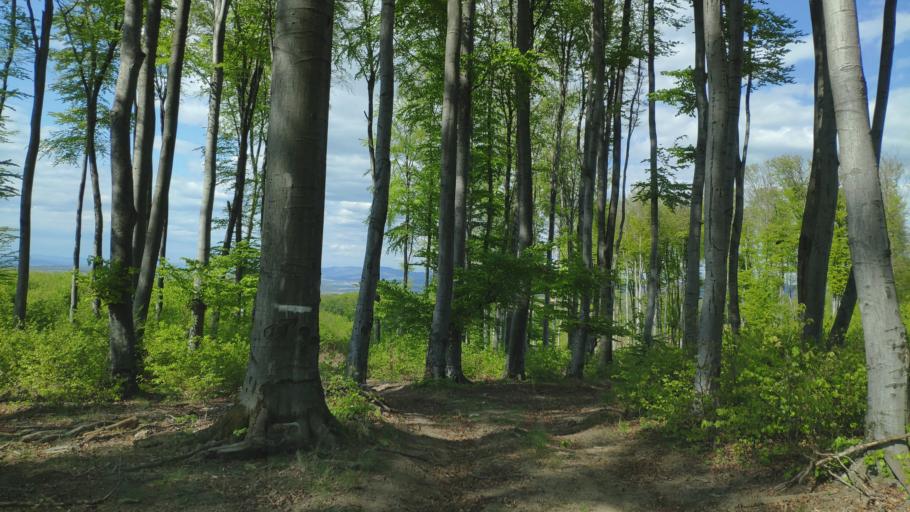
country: SK
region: Kosicky
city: Kosice
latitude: 48.6620
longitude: 21.4486
